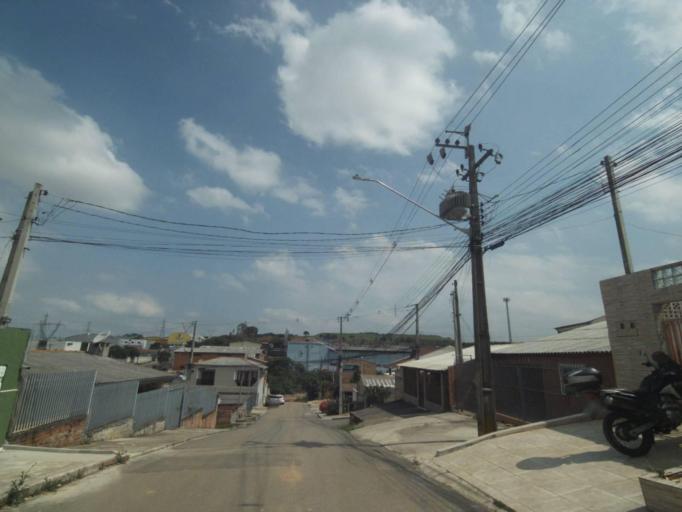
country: BR
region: Parana
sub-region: Curitiba
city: Curitiba
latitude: -25.5025
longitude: -49.3442
